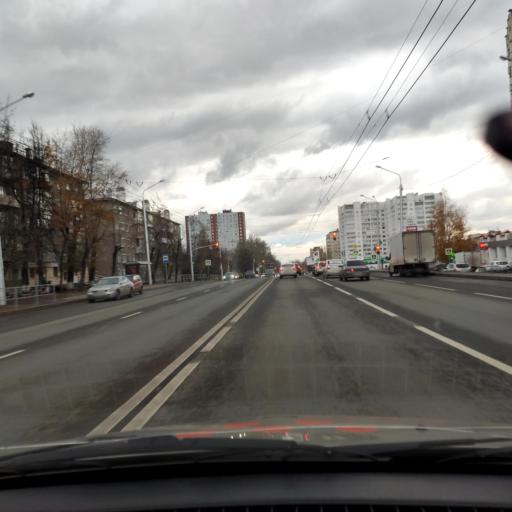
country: RU
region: Bashkortostan
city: Ufa
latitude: 54.7799
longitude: 56.0367
